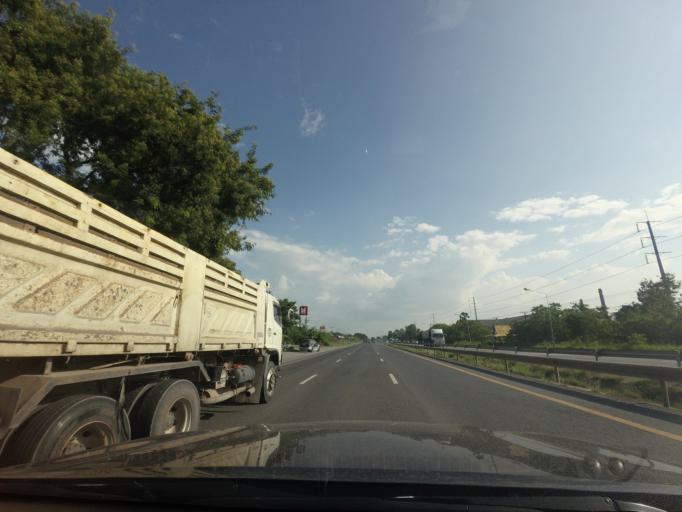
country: TH
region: Sara Buri
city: Chaloem Phra Kiat
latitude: 14.6341
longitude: 100.8883
